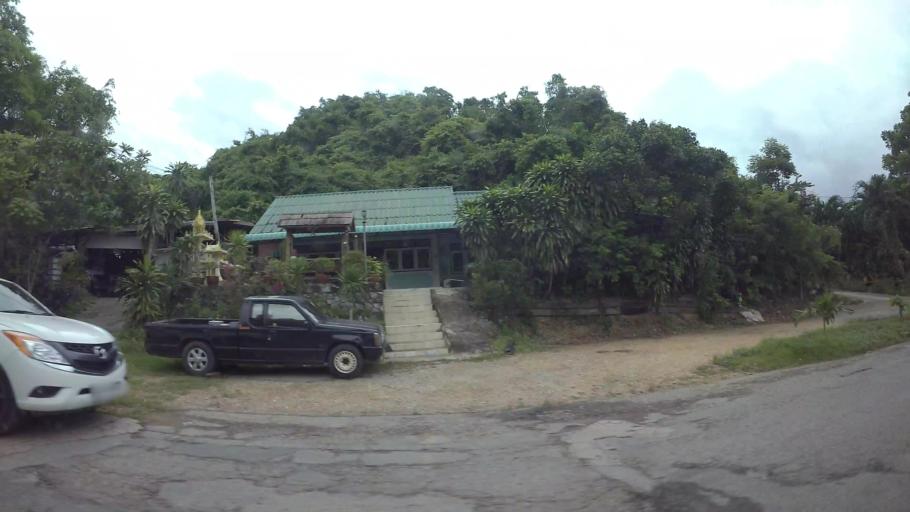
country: TH
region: Chon Buri
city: Si Racha
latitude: 13.2003
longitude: 100.9551
